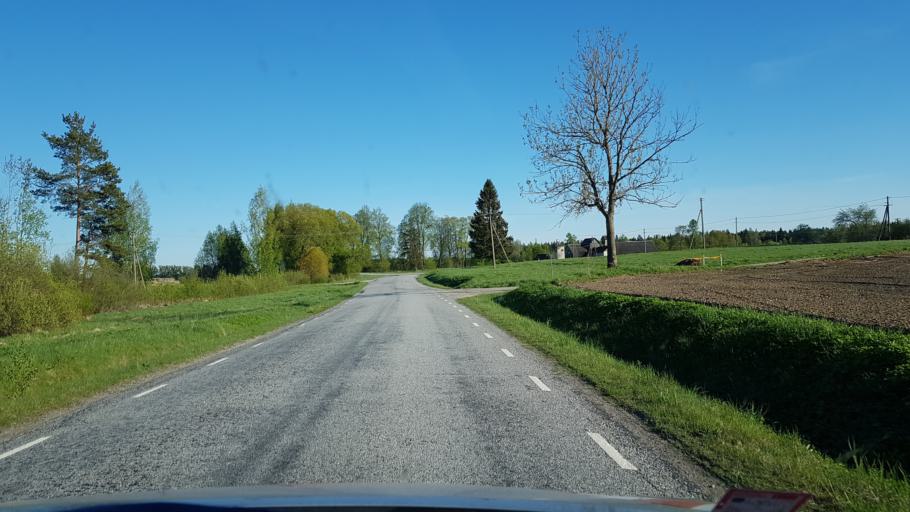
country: EE
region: Vorumaa
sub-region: Voru linn
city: Voru
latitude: 57.9130
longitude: 26.9571
